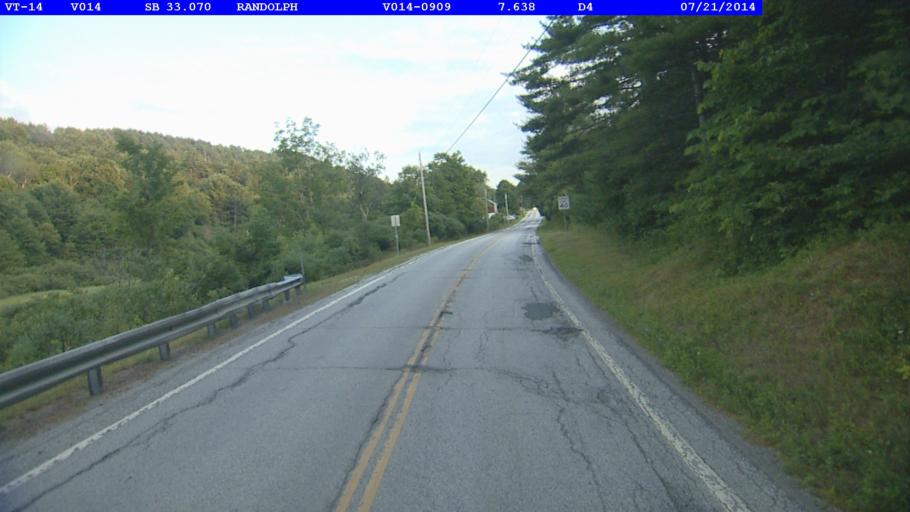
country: US
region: Vermont
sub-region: Orange County
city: Chelsea
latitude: 43.9777
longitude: -72.5565
